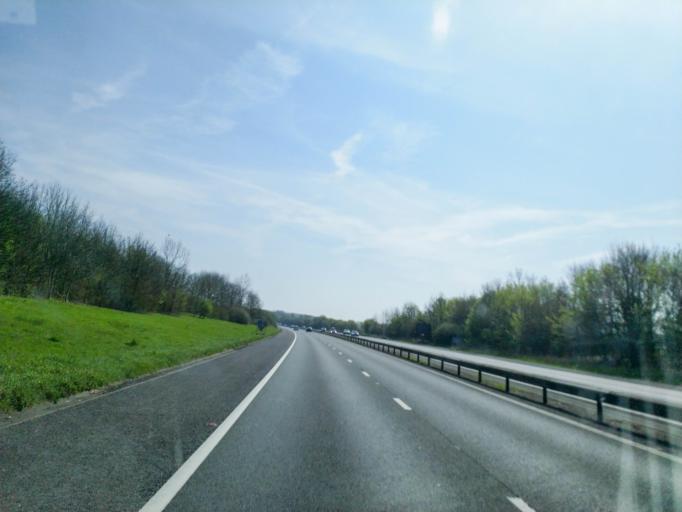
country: GB
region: England
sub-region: Kent
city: Kemsing
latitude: 51.3020
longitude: 0.2152
